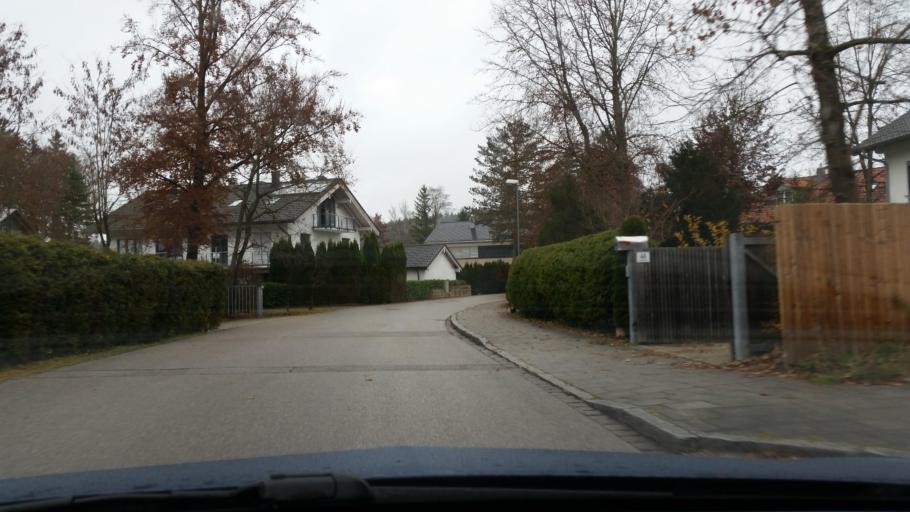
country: DE
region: Bavaria
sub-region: Upper Bavaria
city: Geretsried
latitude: 47.8890
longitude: 11.4651
